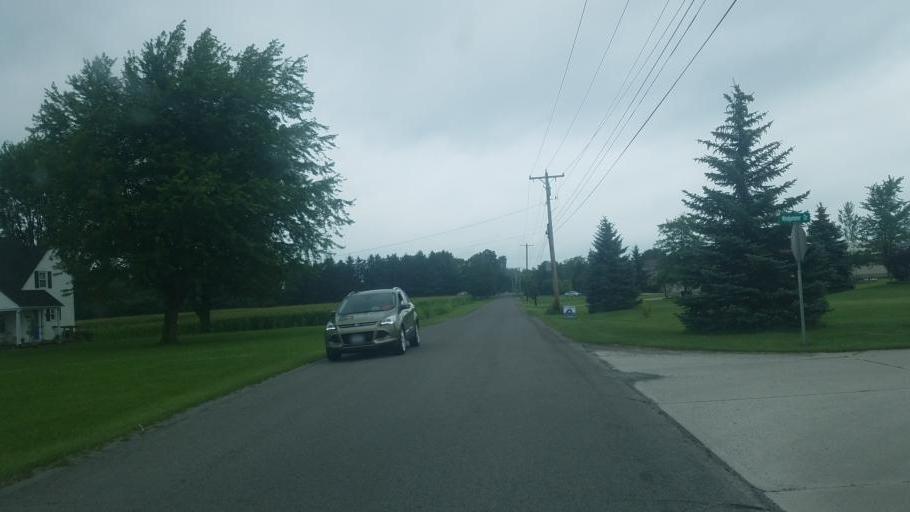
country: US
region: Ohio
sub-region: Logan County
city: Russells Point
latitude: 40.4657
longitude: -83.8578
